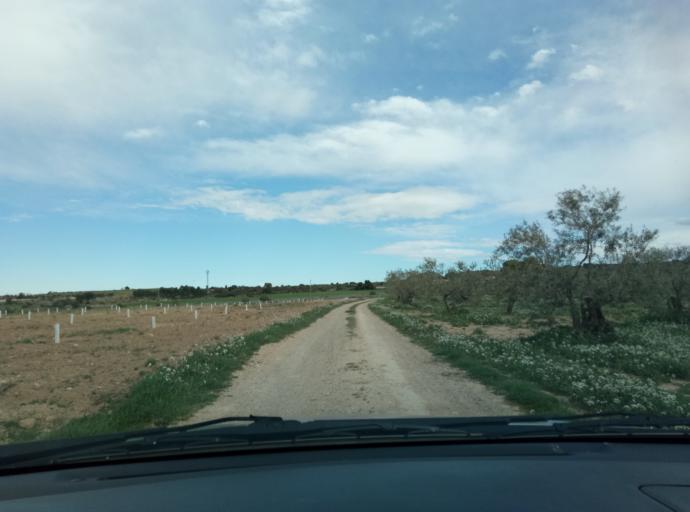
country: ES
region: Catalonia
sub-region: Provincia de Lleida
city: Ciutadilla
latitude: 41.5779
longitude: 1.1246
